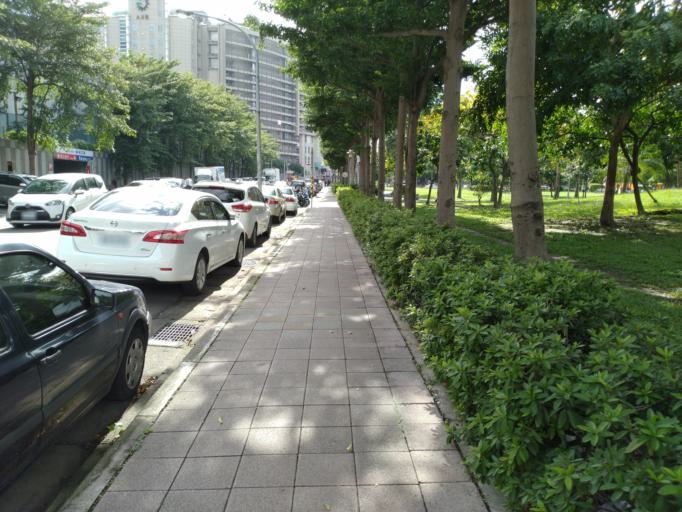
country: TW
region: Taiwan
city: Taoyuan City
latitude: 24.9743
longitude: 121.2535
